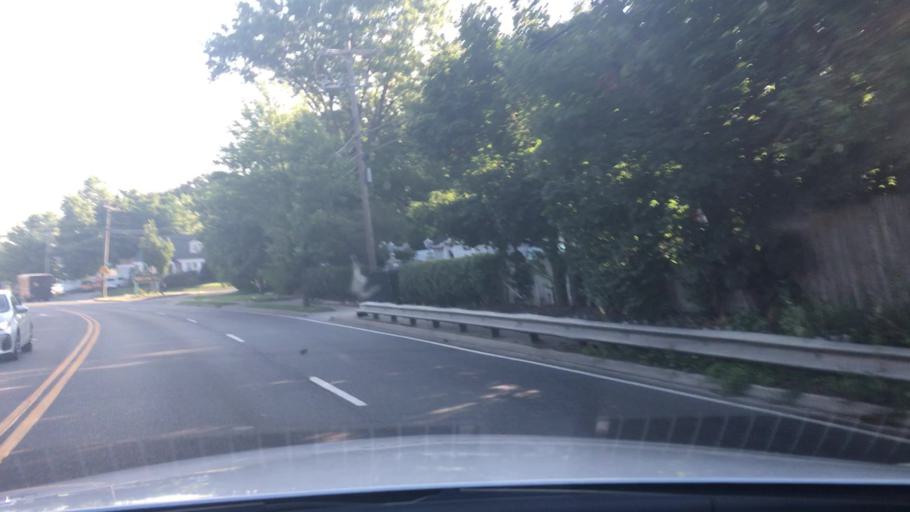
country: US
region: New York
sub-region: Nassau County
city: New Cassel
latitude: 40.7614
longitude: -73.5755
